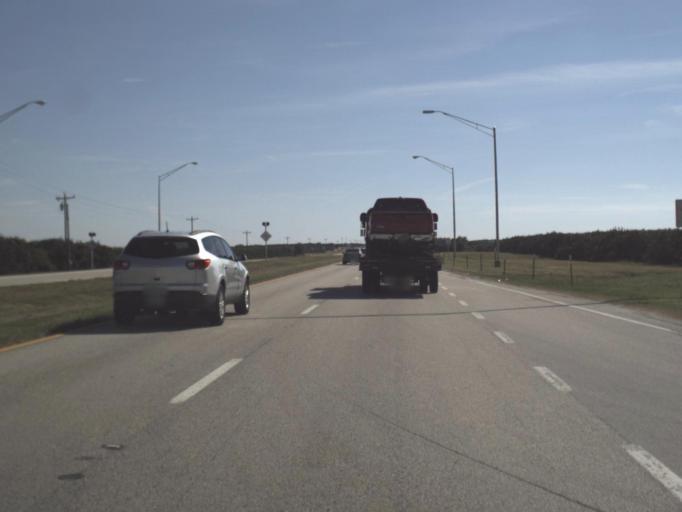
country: US
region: Florida
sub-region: Highlands County
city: Placid Lakes
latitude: 27.2076
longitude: -81.3288
